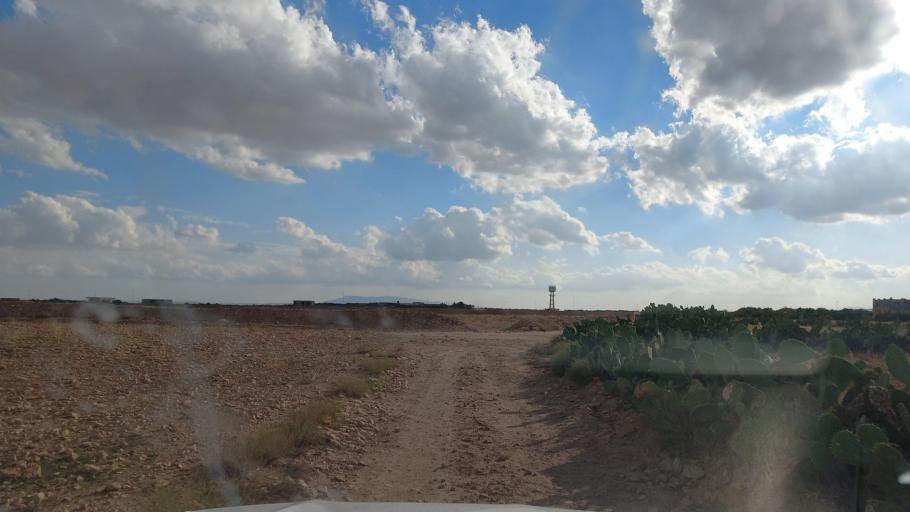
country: TN
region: Al Qasrayn
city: Sbiba
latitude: 35.3871
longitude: 9.0701
